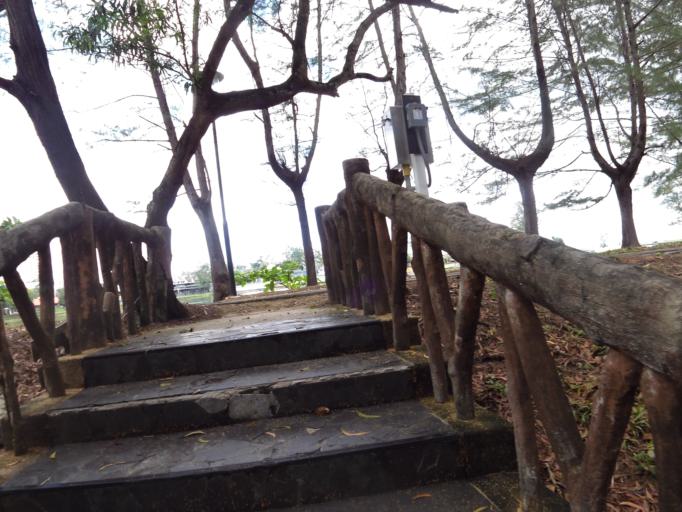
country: TH
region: Phuket
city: Ban Karon
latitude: 7.8534
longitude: 98.2937
